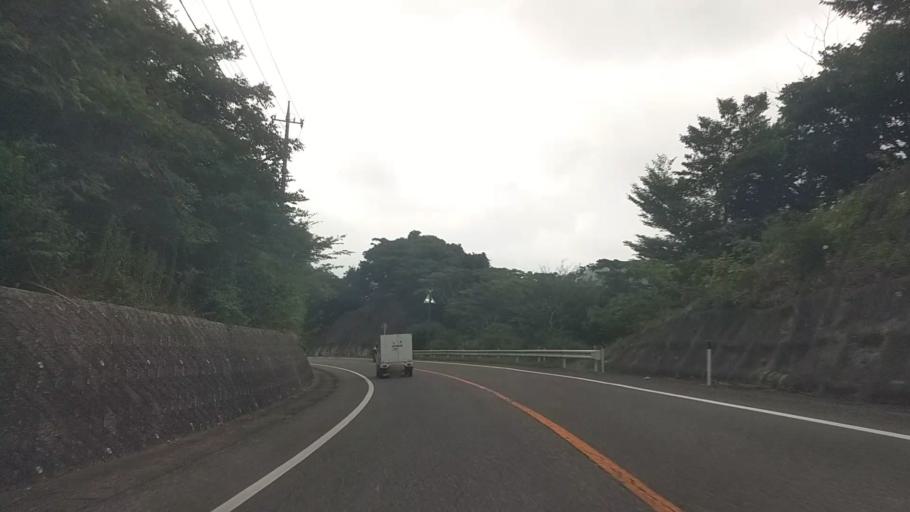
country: JP
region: Chiba
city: Kawaguchi
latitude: 35.1548
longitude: 140.0671
